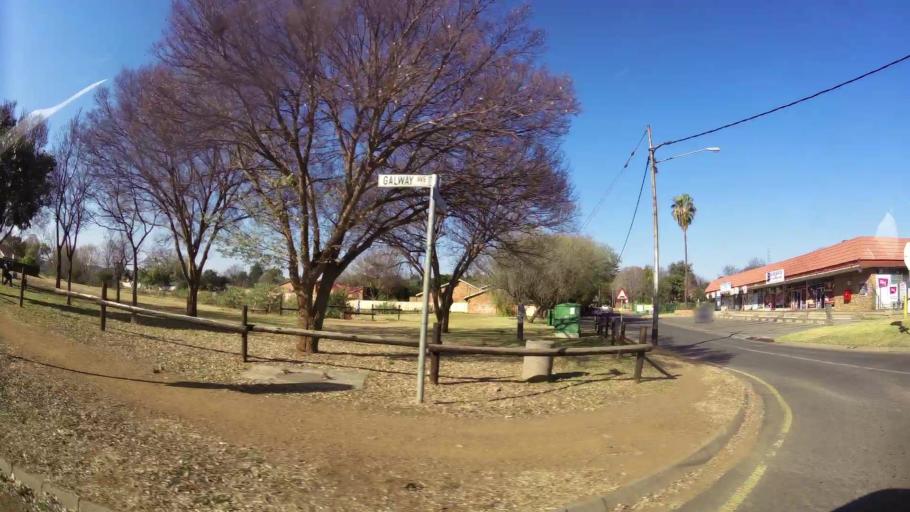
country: ZA
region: Gauteng
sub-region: City of Tshwane Metropolitan Municipality
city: Centurion
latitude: -25.8588
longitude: 28.1671
